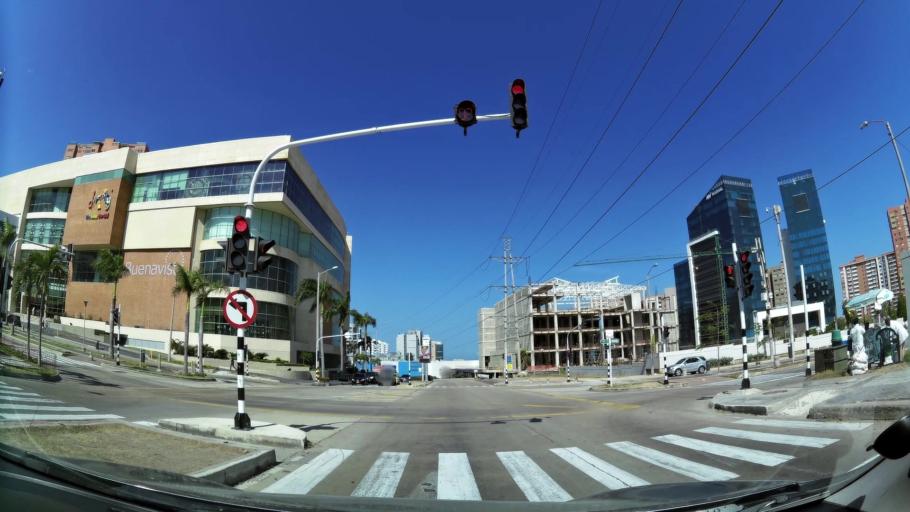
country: CO
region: Atlantico
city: Barranquilla
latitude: 11.0143
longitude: -74.8272
